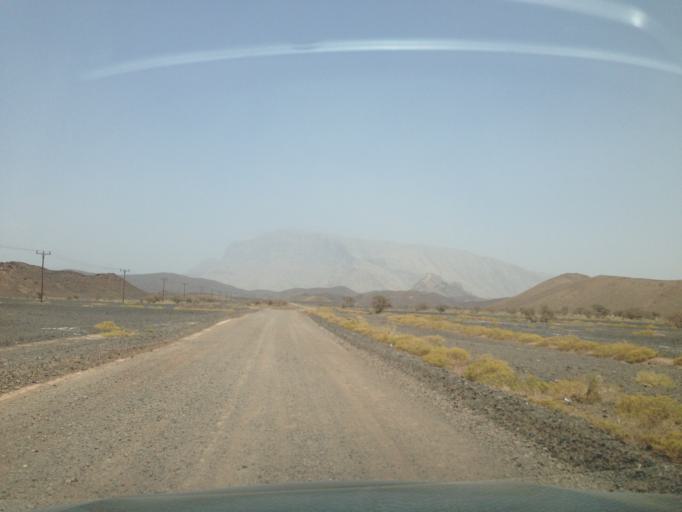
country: OM
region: Az Zahirah
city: `Ibri
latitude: 23.2072
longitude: 56.8481
